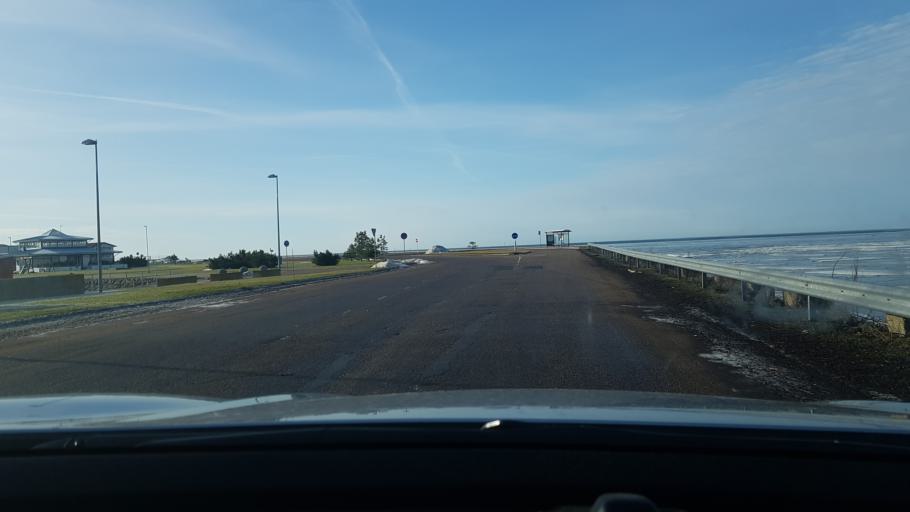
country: EE
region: Saare
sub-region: Kuressaare linn
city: Kuressaare
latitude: 58.2179
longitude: 22.5048
